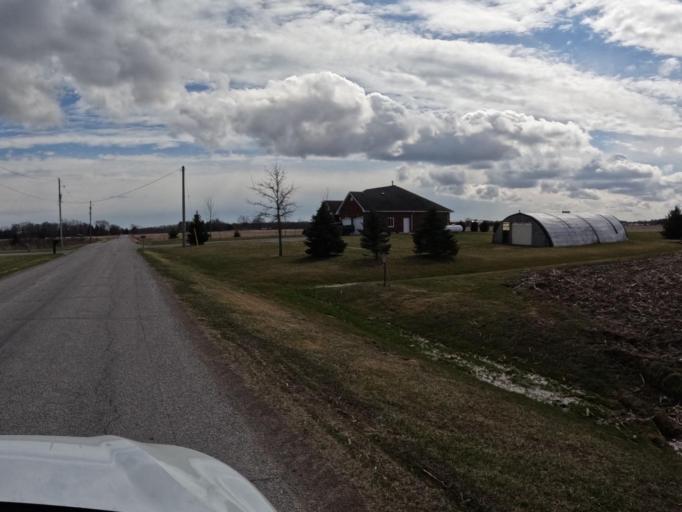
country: CA
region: Ontario
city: Norfolk County
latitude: 42.8705
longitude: -80.1939
